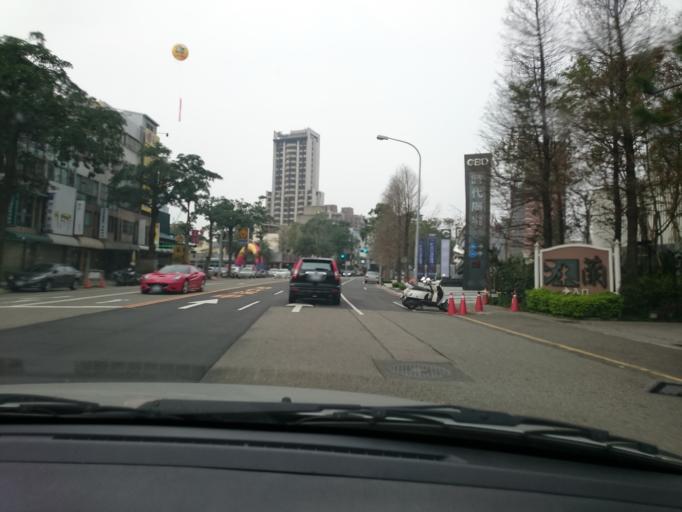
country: TW
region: Taiwan
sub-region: Taichung City
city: Taichung
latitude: 24.1621
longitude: 120.6351
